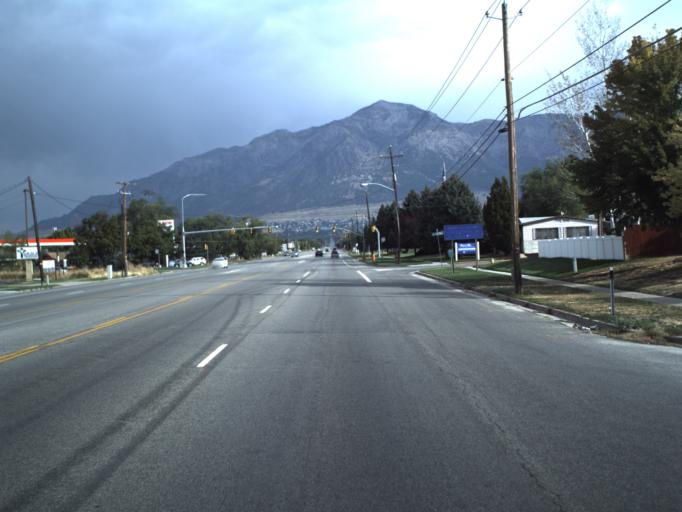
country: US
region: Utah
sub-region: Weber County
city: Harrisville
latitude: 41.2733
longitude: -111.9693
